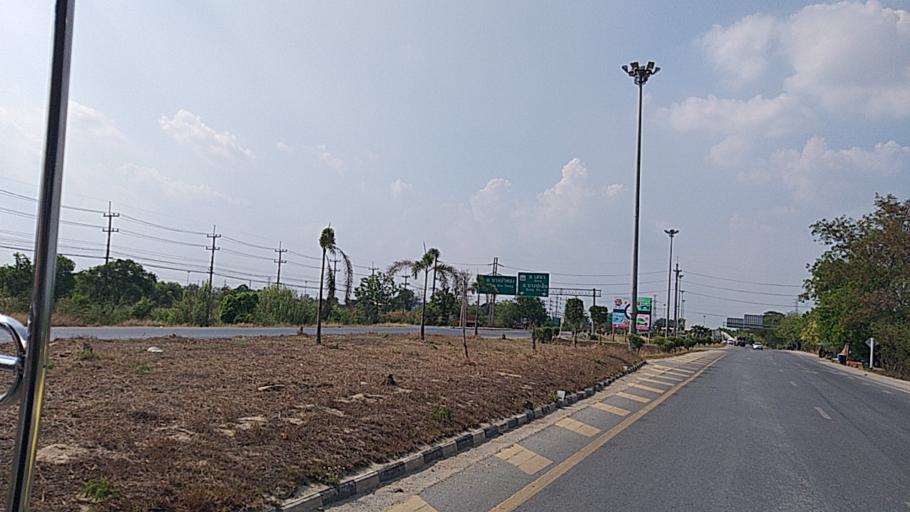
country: TH
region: Pathum Thani
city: Sam Khok
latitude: 14.0862
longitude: 100.5199
